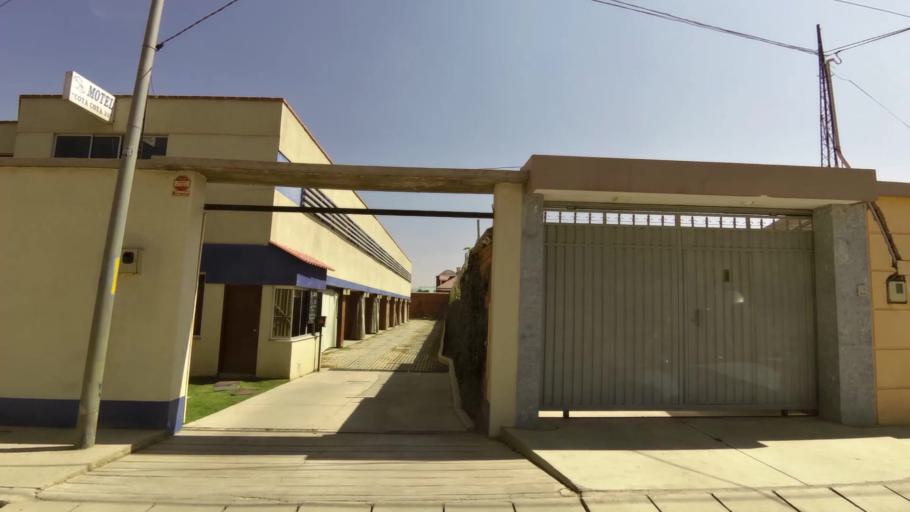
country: BO
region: La Paz
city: La Paz
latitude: -16.5446
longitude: -68.0595
